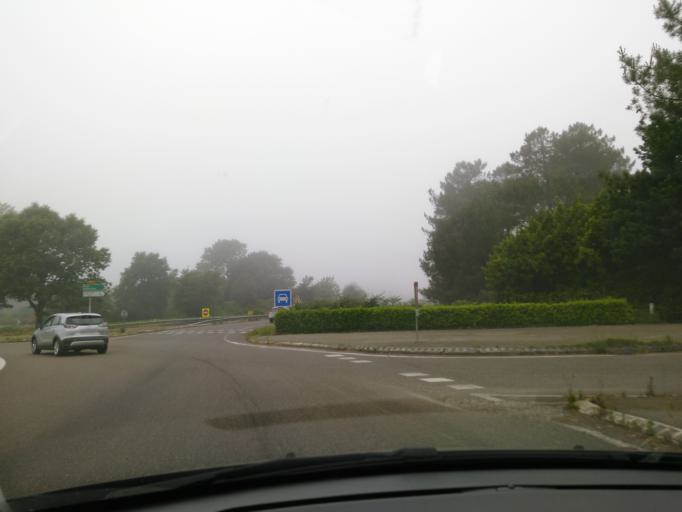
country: FR
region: Aquitaine
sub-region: Departement des Landes
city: Begaar
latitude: 43.8298
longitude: -0.8337
